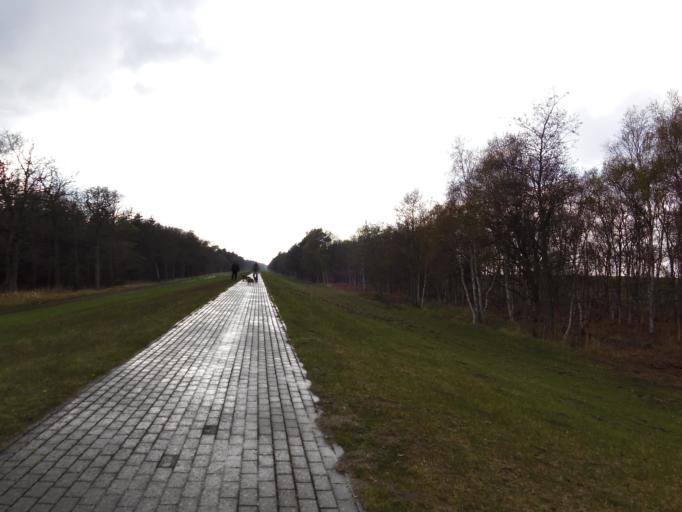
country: DE
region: Mecklenburg-Vorpommern
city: Zingst
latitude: 54.4409
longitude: 12.7701
